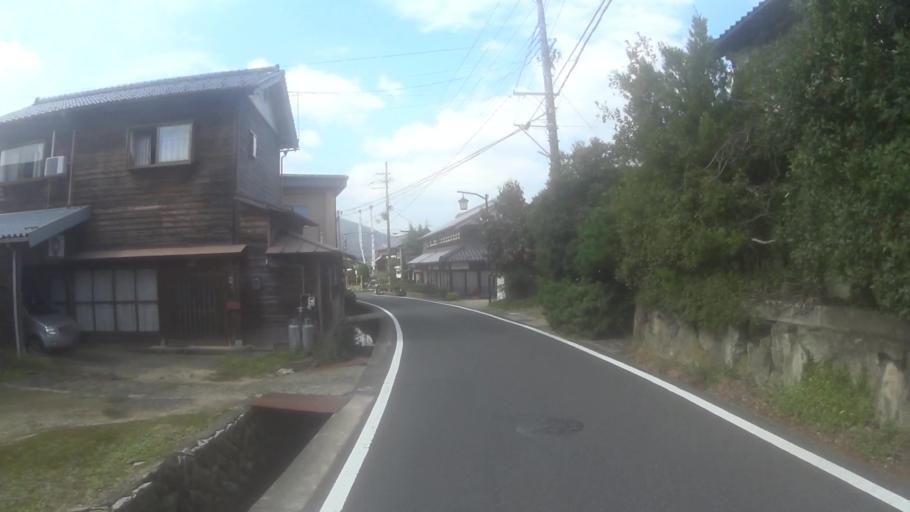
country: JP
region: Kyoto
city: Miyazu
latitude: 35.5870
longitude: 135.1036
